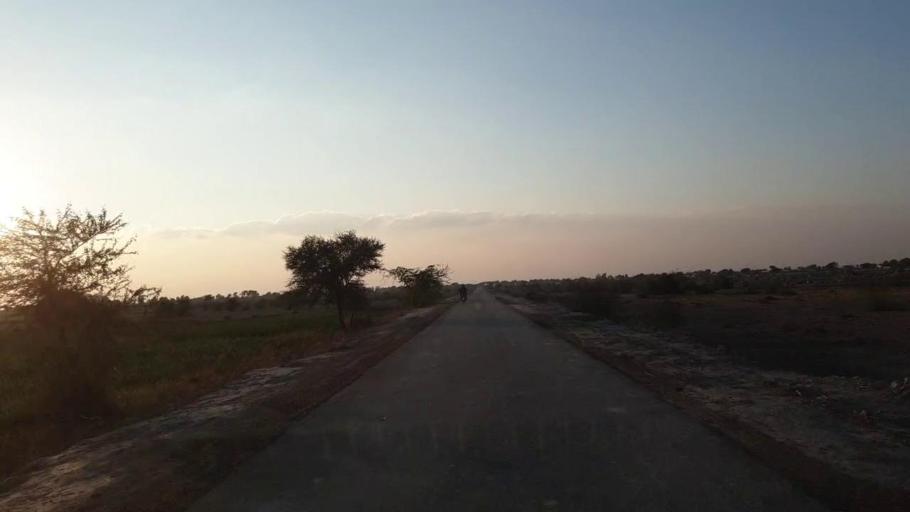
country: PK
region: Sindh
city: Shahpur Chakar
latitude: 26.1566
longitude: 68.5528
